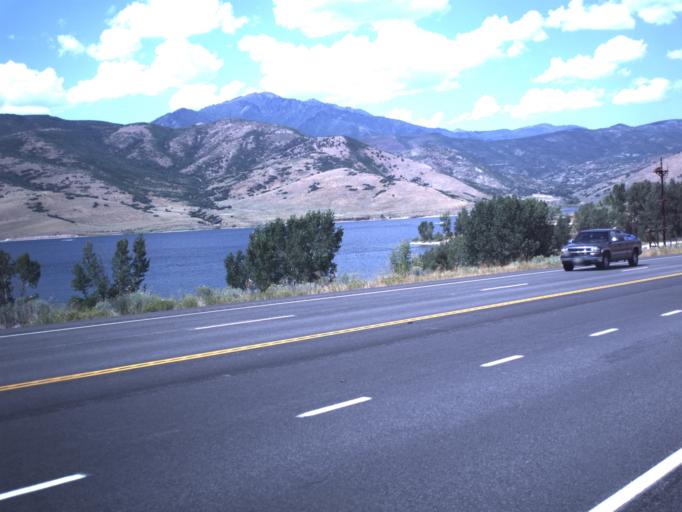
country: US
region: Utah
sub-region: Wasatch County
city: Midway
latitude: 40.4255
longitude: -111.4897
